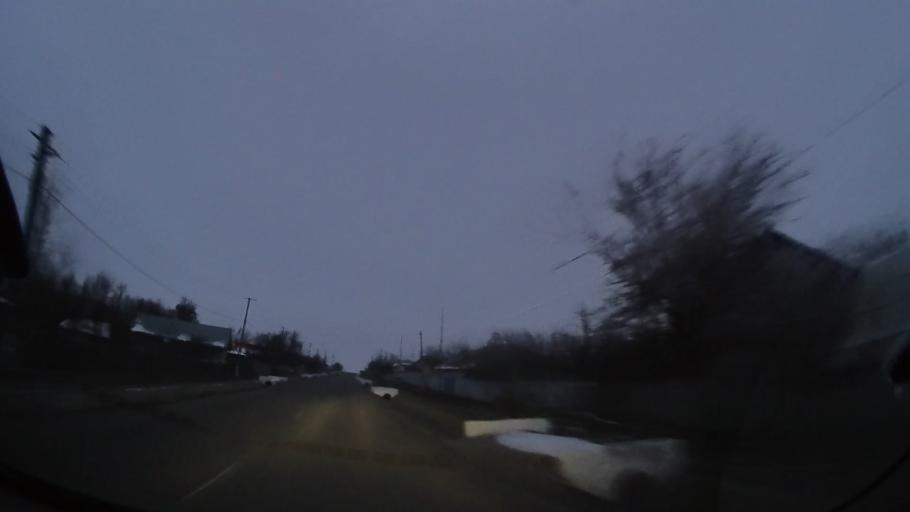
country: RO
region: Vaslui
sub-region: Comuna Dimitrie Cantemir
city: Dimitrie Cantemir
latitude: 46.4629
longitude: 28.0323
